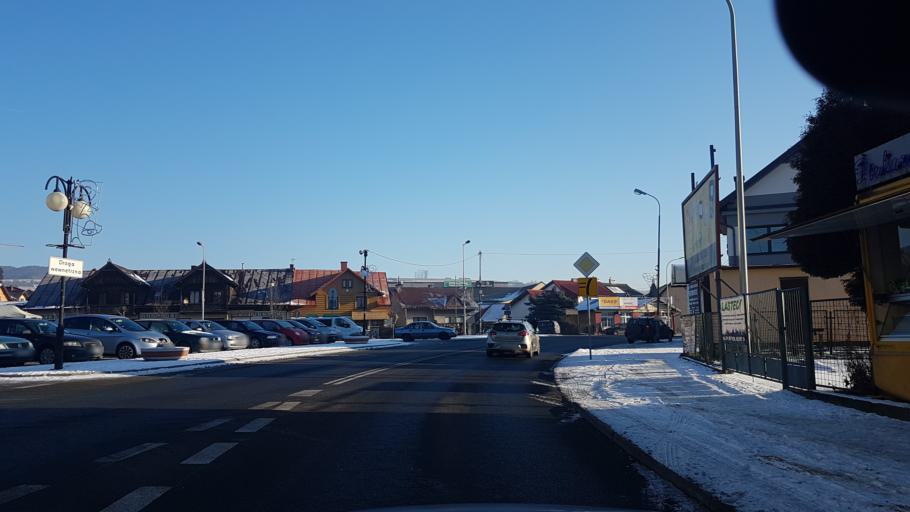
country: PL
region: Lesser Poland Voivodeship
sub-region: Powiat nowosadecki
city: Lacko
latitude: 49.5570
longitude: 20.4349
